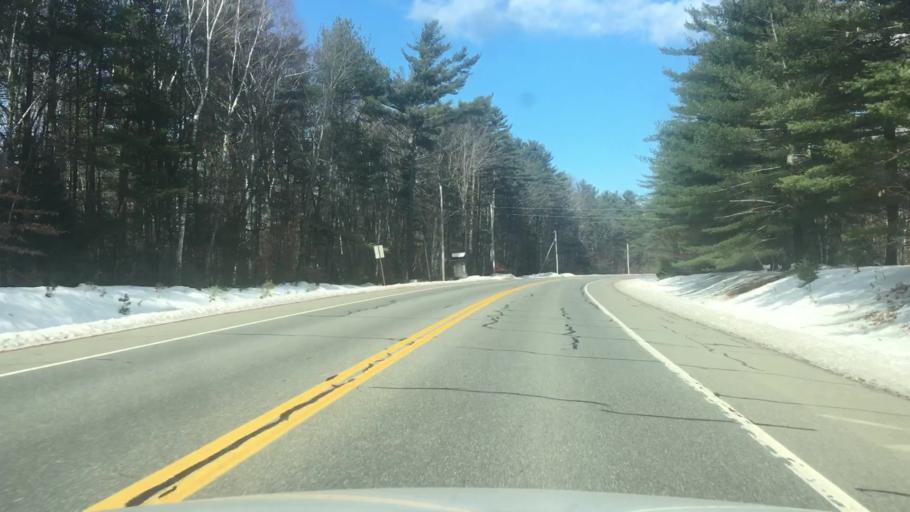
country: US
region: Maine
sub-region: Somerset County
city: Madison
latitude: 44.9804
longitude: -69.8672
